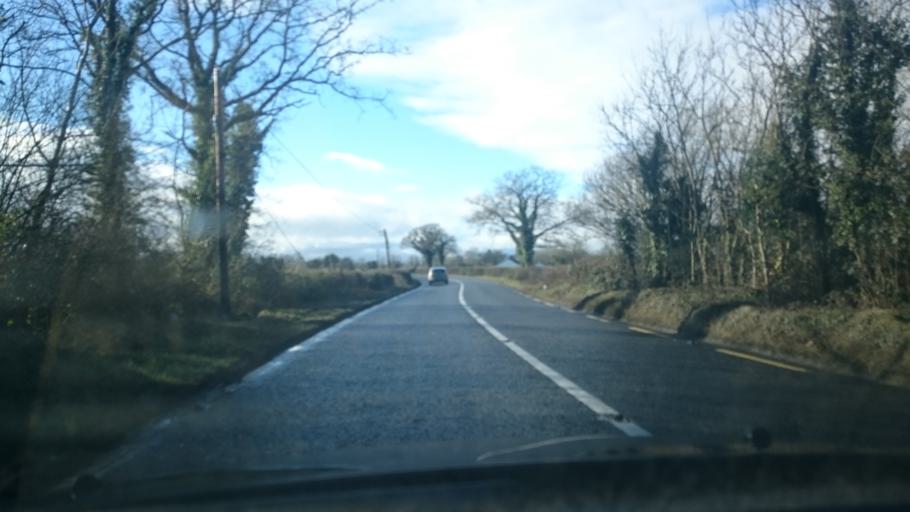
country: IE
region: Leinster
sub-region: Kilkenny
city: Callan
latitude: 52.5795
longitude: -7.3199
